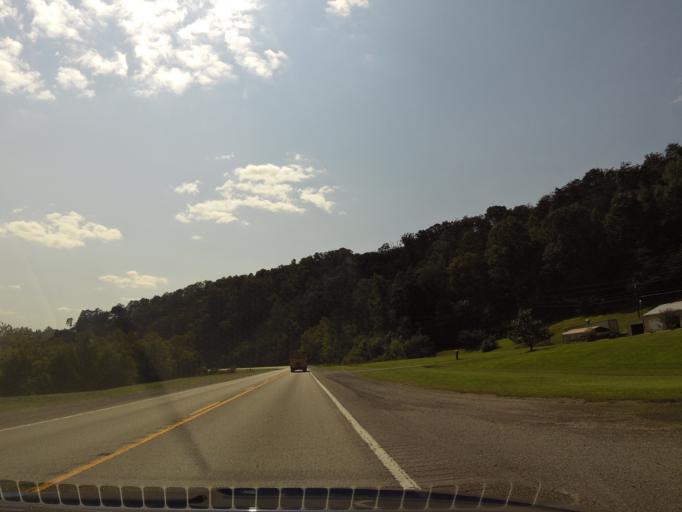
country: US
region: Kentucky
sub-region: Harlan County
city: Loyall
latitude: 36.8212
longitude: -83.4912
